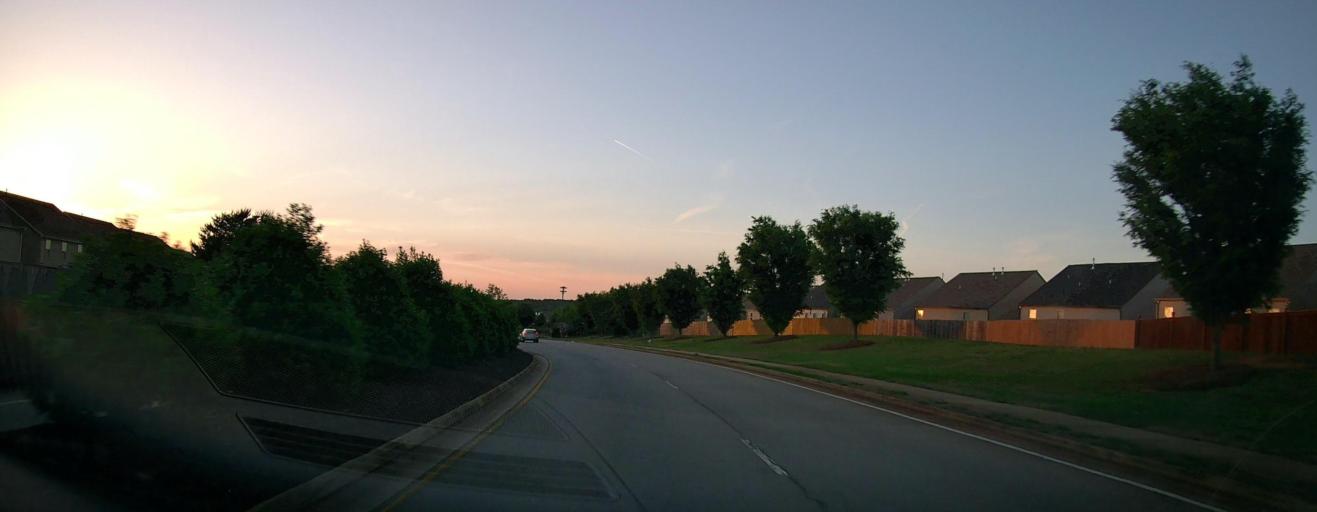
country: US
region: Georgia
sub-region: Henry County
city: McDonough
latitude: 33.4456
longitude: -84.1880
